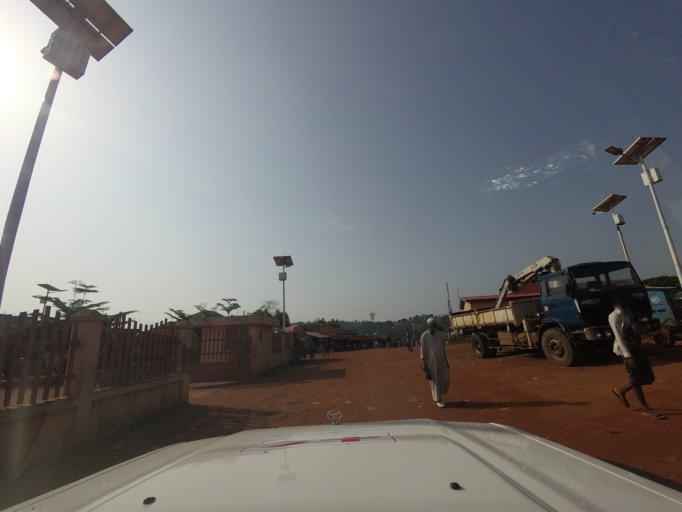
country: GN
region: Nzerekore
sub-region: Prefecture de Guekedou
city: Gueckedou
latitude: 8.5608
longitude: -10.1343
